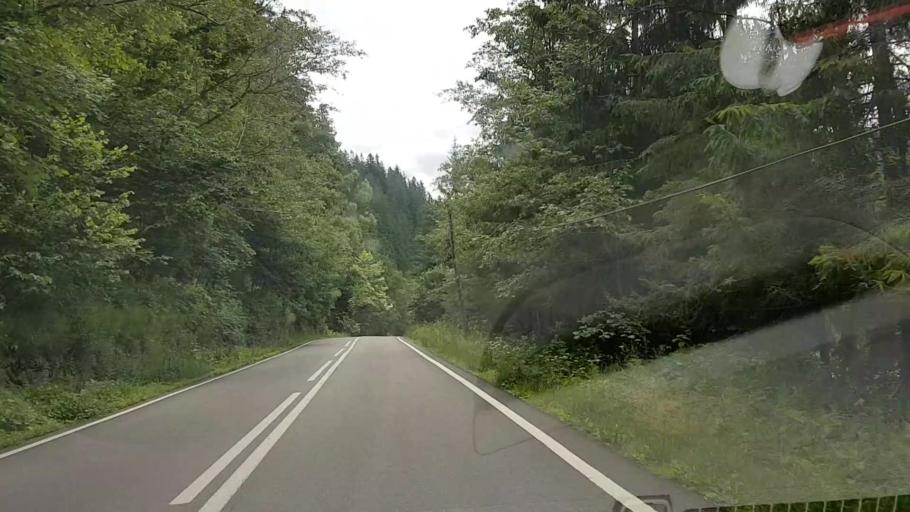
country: RO
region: Suceava
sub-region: Comuna Crucea
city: Crucea
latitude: 47.3665
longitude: 25.5909
